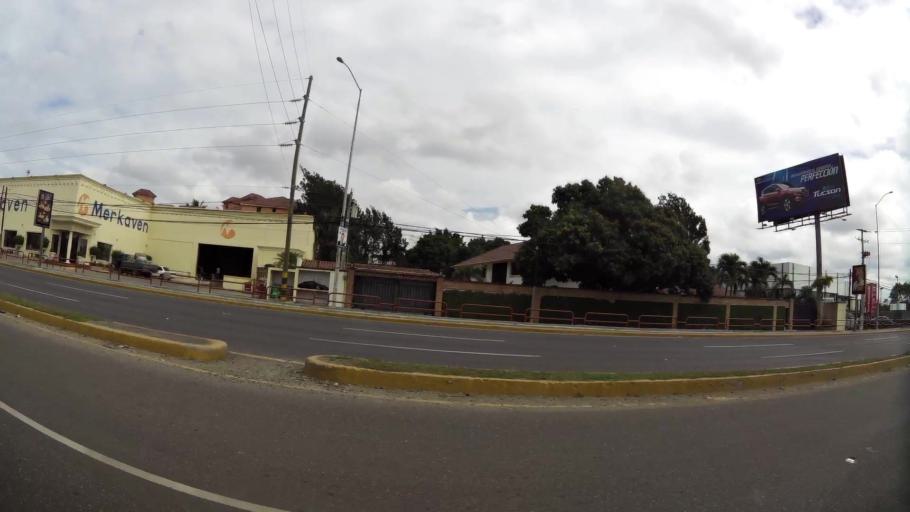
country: DO
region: Santiago
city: Santiago de los Caballeros
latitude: 19.4481
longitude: -70.6773
